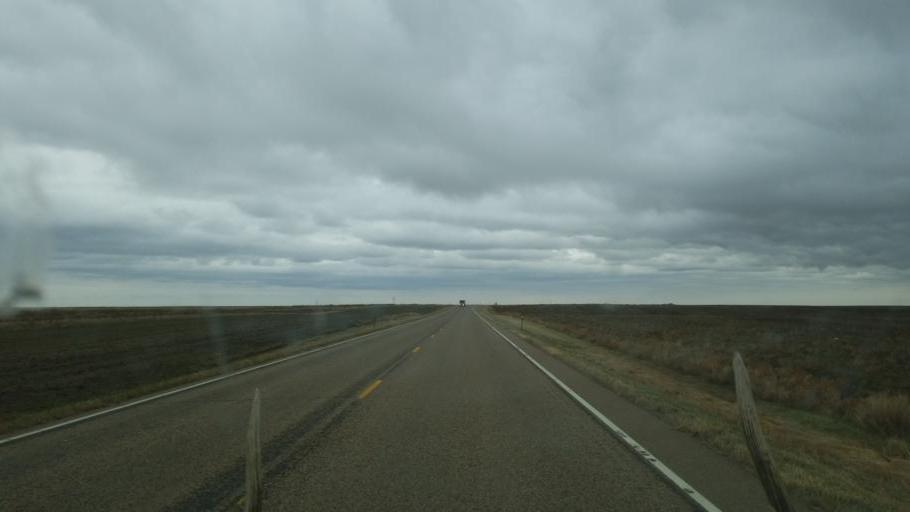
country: US
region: Colorado
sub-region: Cheyenne County
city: Cheyenne Wells
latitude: 38.8173
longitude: -102.4991
